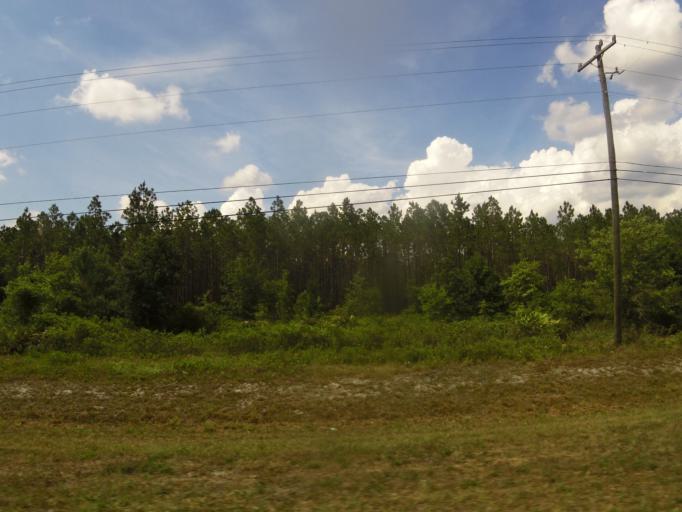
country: US
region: Florida
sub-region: Baker County
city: Macclenny
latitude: 30.2013
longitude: -82.0378
